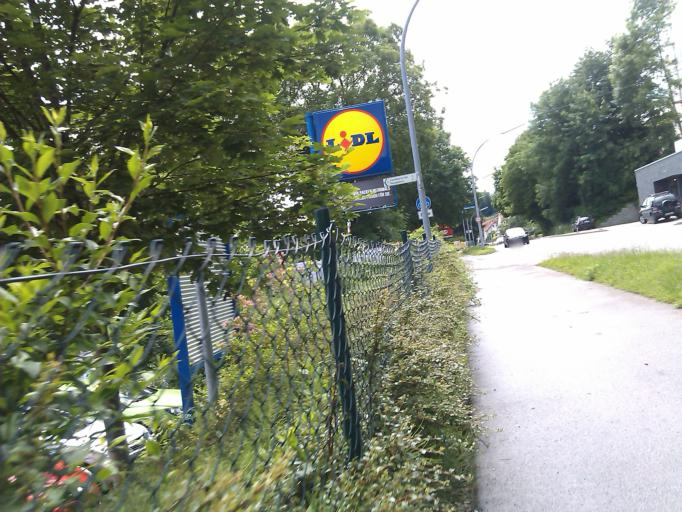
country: DE
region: Bavaria
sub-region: Swabia
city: Kaufbeuren
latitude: 47.8927
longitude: 10.6117
